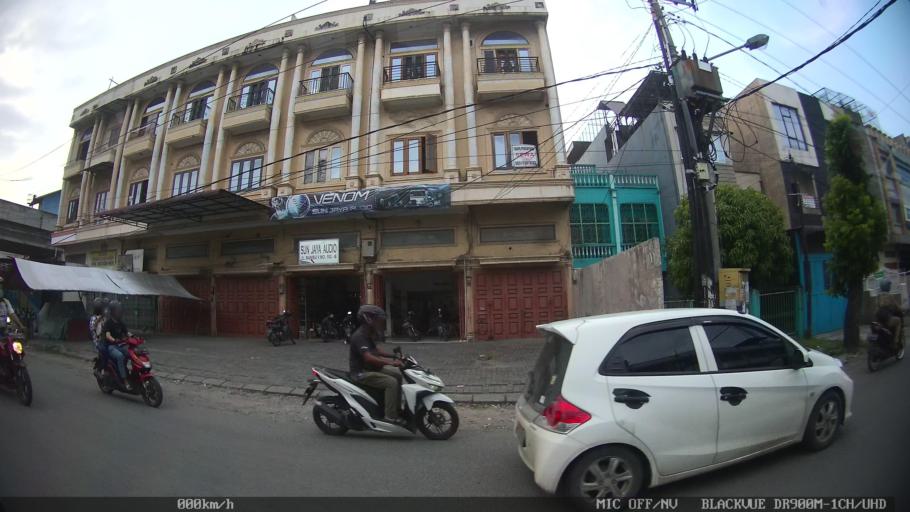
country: ID
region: North Sumatra
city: Medan
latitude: 3.6068
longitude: 98.6755
